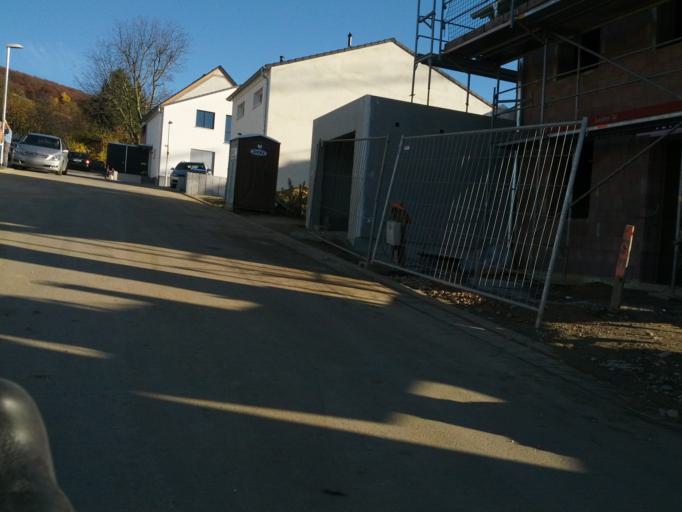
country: DE
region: Baden-Wuerttemberg
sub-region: Freiburg Region
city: Pfaffenweiler
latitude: 47.9424
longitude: 7.7569
